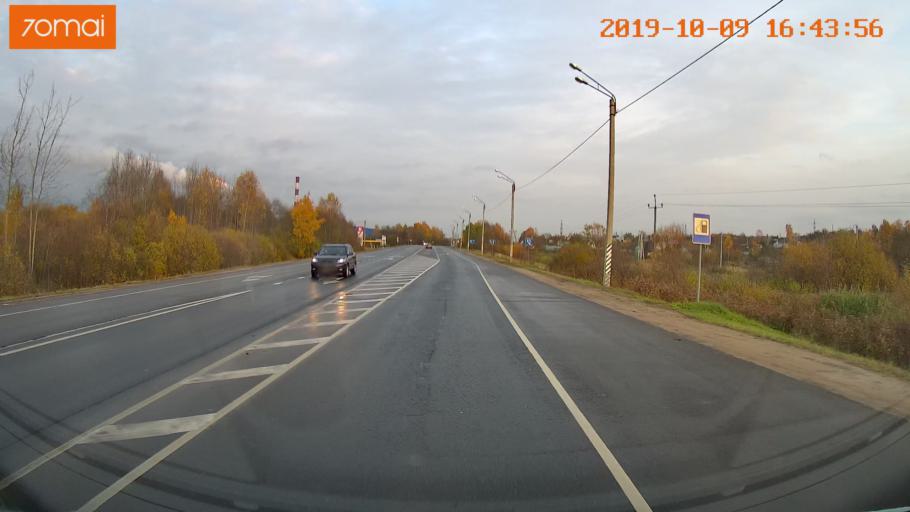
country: RU
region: Kostroma
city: Volgorechensk
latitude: 57.4525
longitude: 41.1328
